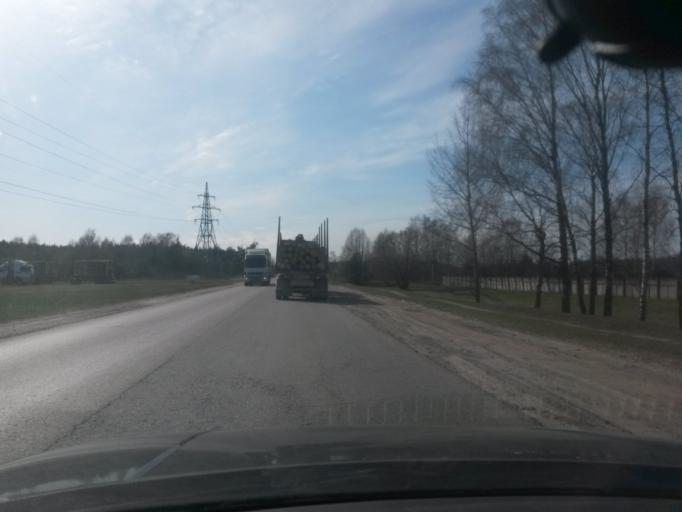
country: LV
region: Stopini
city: Ulbroka
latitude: 56.9132
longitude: 24.2418
